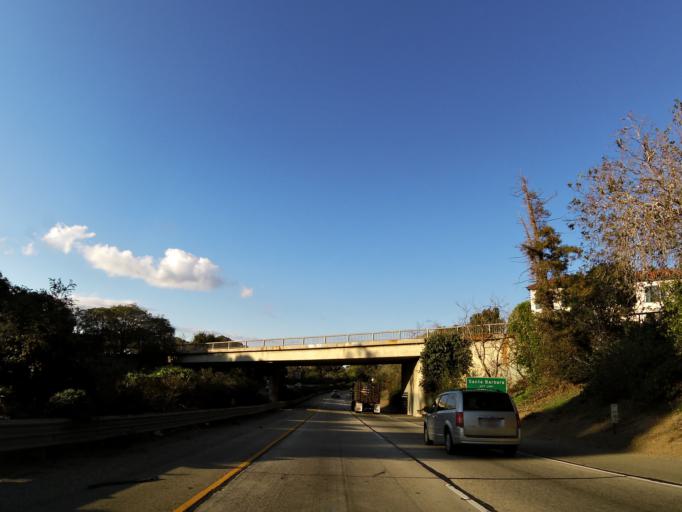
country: US
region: California
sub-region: Santa Barbara County
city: Montecito
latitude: 34.4213
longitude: -119.6393
